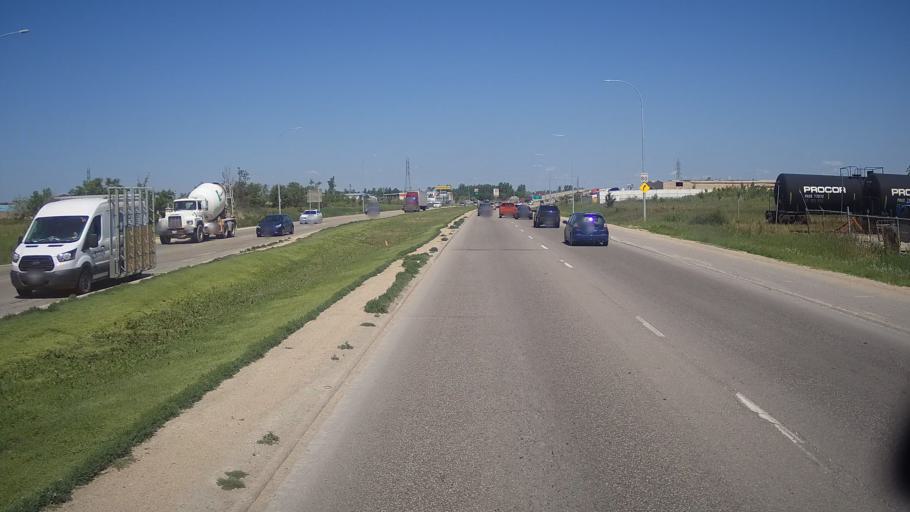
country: CA
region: Manitoba
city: Winnipeg
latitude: 49.8869
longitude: -97.0722
